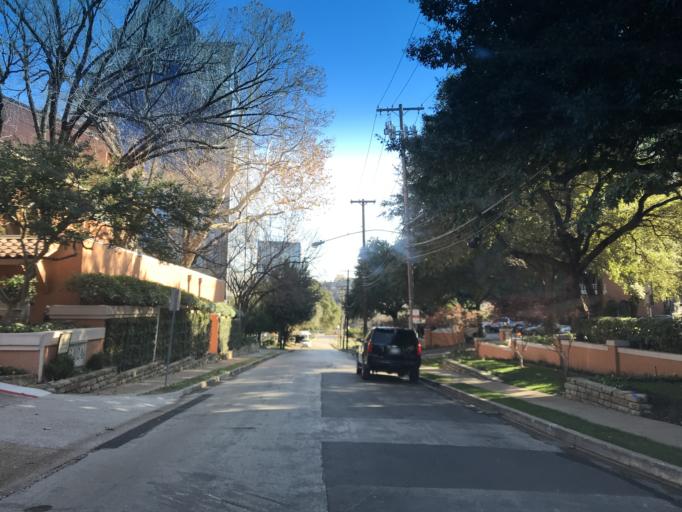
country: US
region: Texas
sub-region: Dallas County
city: Dallas
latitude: 32.8049
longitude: -96.8073
